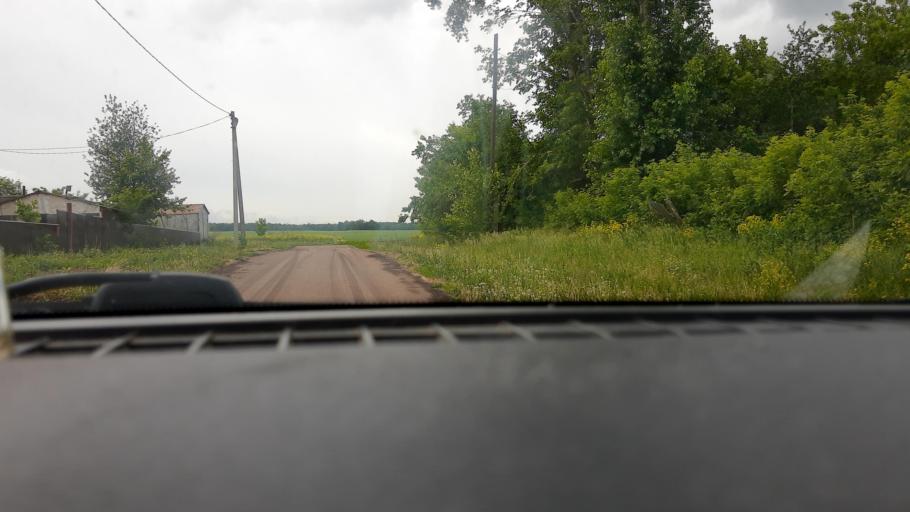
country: RU
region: Bashkortostan
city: Dmitriyevka
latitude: 54.7178
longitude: 55.4875
